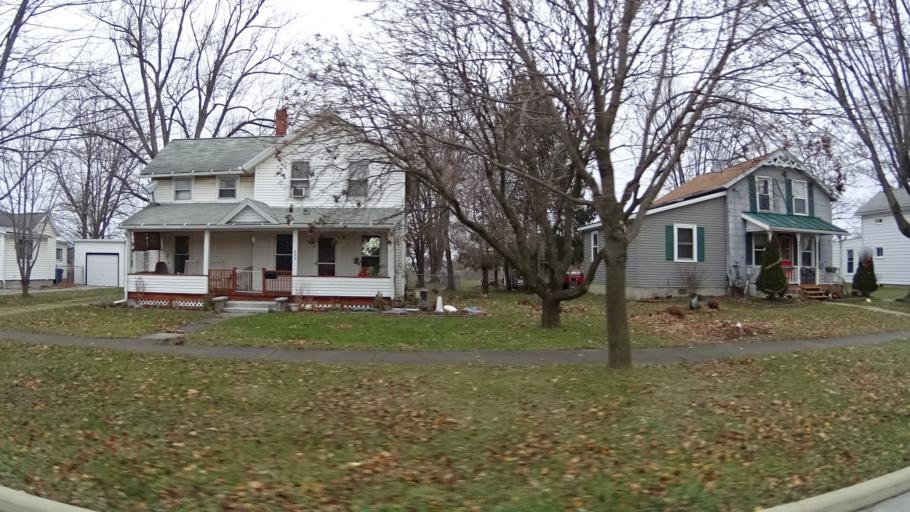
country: US
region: Ohio
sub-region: Lorain County
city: Wellington
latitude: 41.1688
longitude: -82.2280
